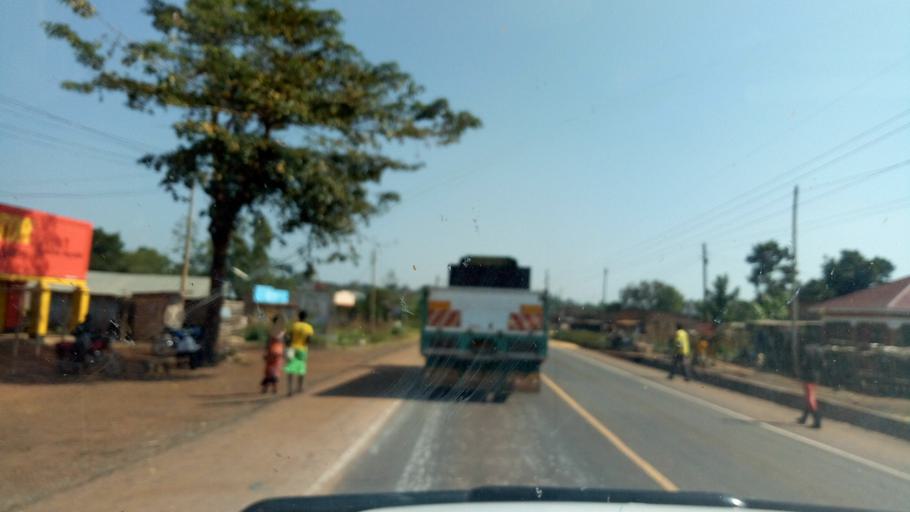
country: UG
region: Western Region
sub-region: Kiryandongo District
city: Kiryandongo
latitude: 1.9414
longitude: 32.1308
